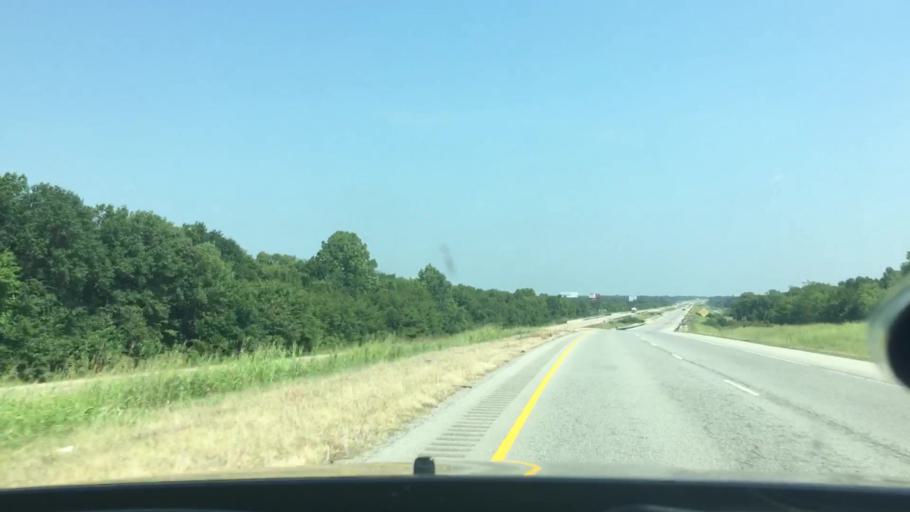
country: US
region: Oklahoma
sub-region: Atoka County
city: Atoka
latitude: 34.2379
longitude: -96.2205
